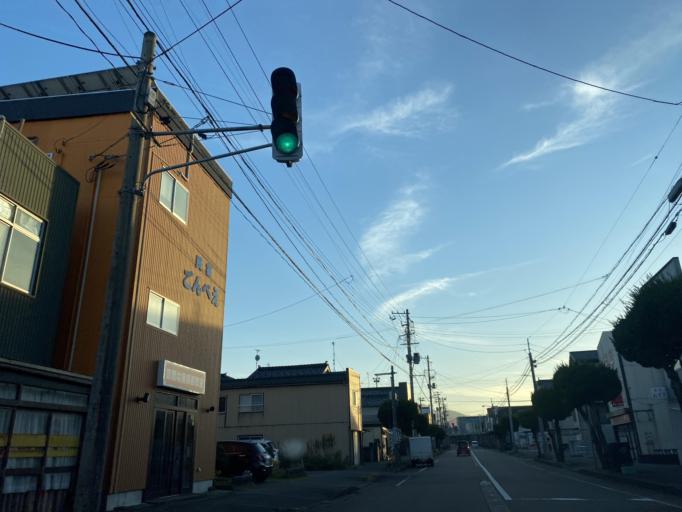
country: JP
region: Niigata
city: Kashiwazaki
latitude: 37.3754
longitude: 138.5642
